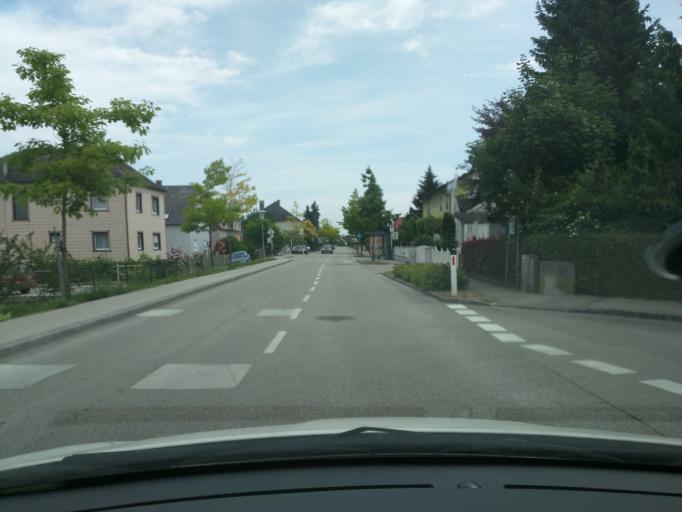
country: AT
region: Lower Austria
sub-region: Politischer Bezirk Amstetten
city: Winklarn
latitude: 48.1089
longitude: 14.8394
